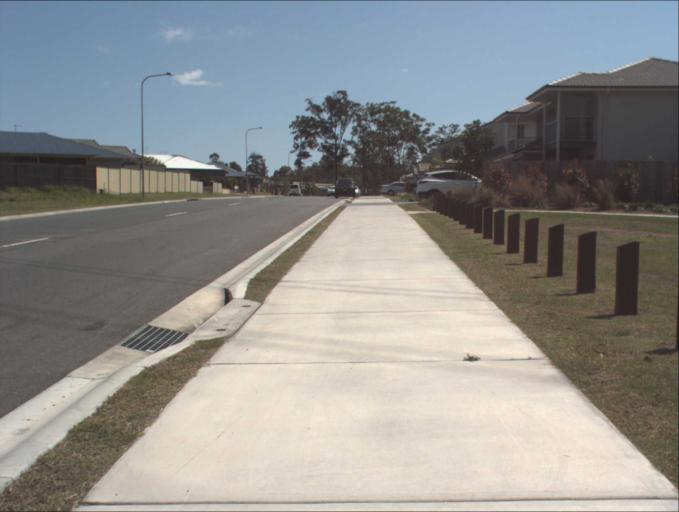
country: AU
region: Queensland
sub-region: Logan
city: Woodridge
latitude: -27.6606
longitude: 153.0867
